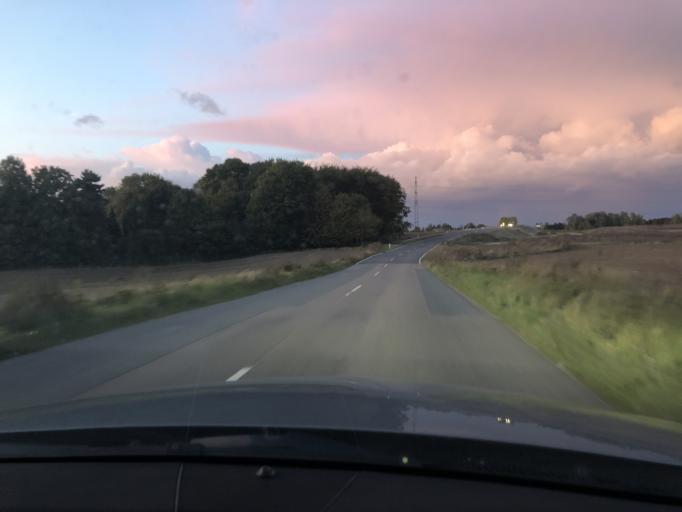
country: DK
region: Zealand
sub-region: Soro Kommune
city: Stenlille
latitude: 55.6563
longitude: 11.6123
